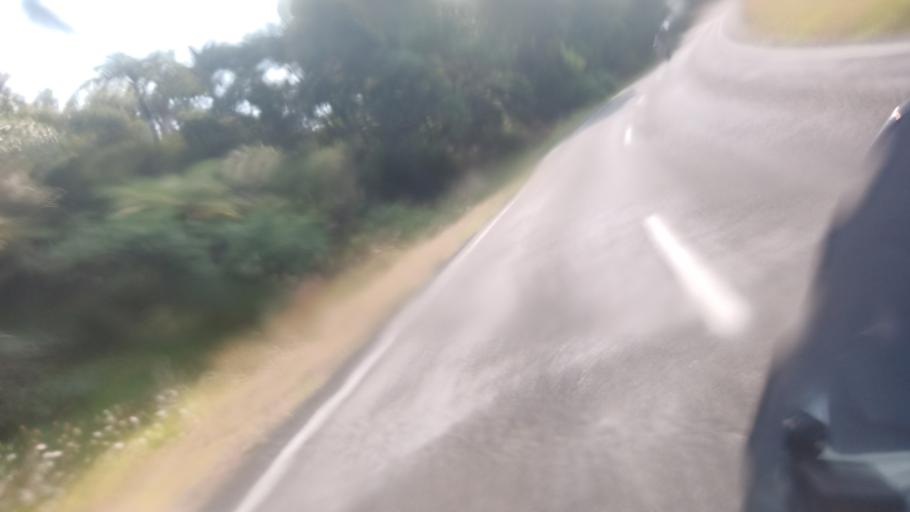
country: NZ
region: Bay of Plenty
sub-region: Opotiki District
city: Opotiki
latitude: -37.6752
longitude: 177.8015
